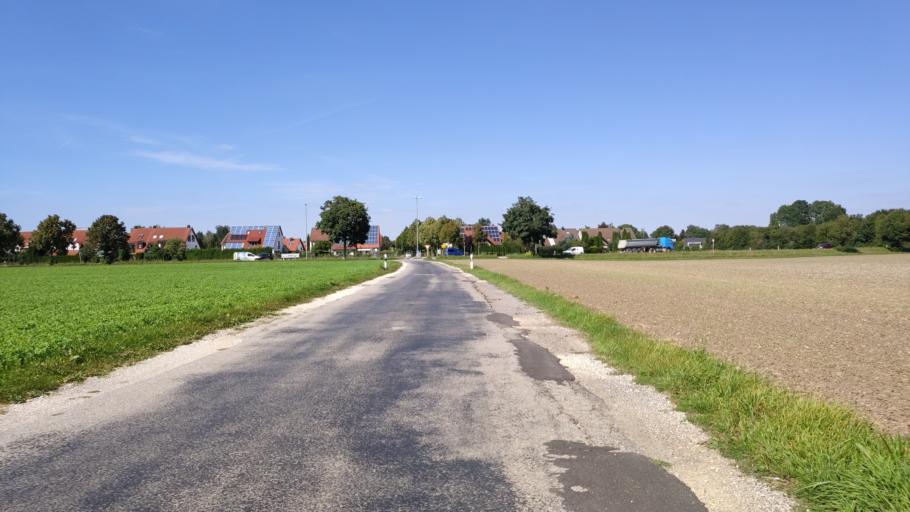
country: DE
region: Bavaria
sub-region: Swabia
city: Konigsbrunn
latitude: 48.2500
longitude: 10.9007
